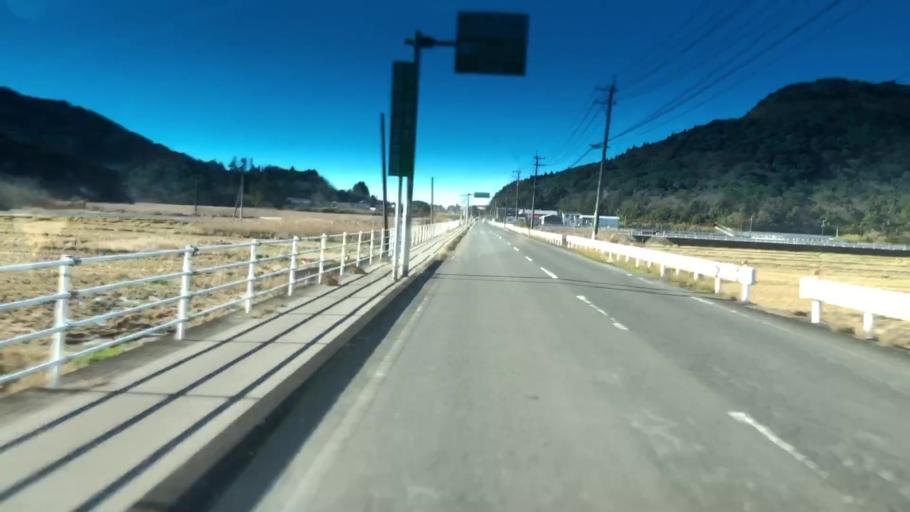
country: JP
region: Kagoshima
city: Satsumasendai
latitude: 31.8171
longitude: 130.2700
